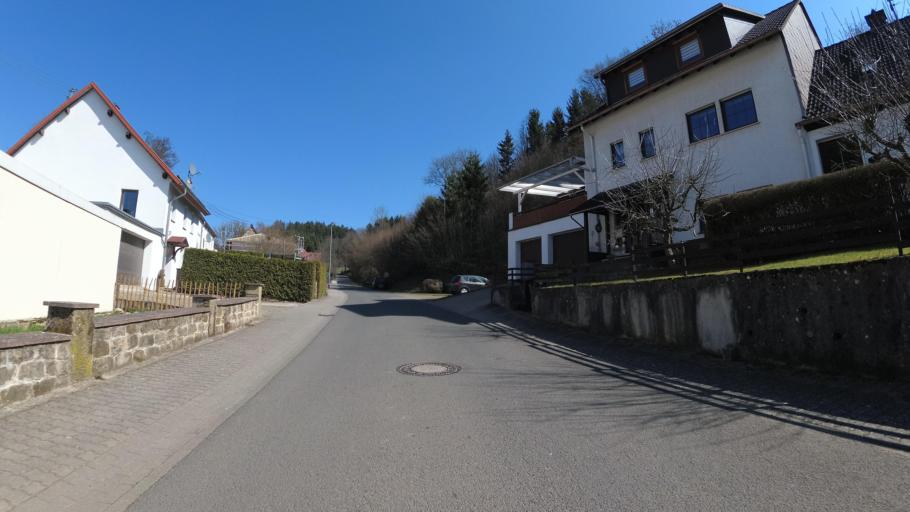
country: DE
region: Rheinland-Pfalz
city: Thallichtenberg
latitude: 49.5586
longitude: 7.3537
